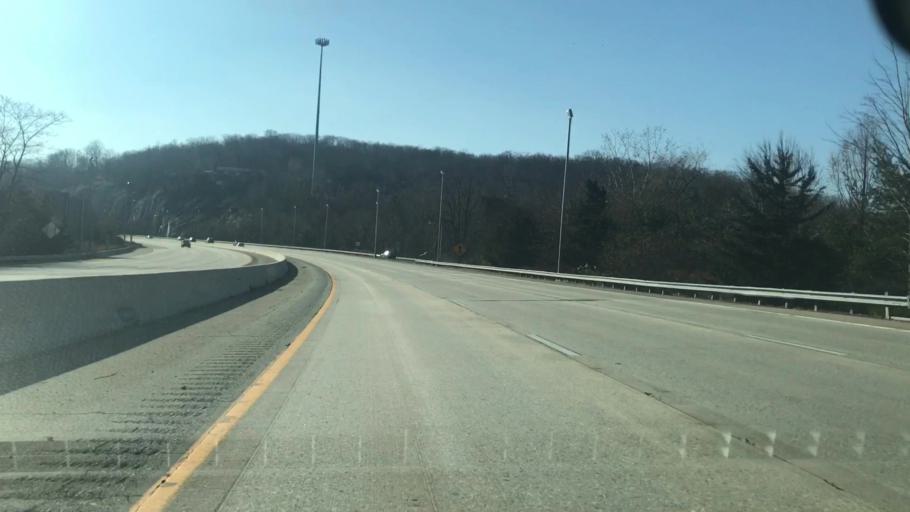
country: US
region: New Jersey
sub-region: Passaic County
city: Pompton Lakes
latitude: 41.0159
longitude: -74.2960
